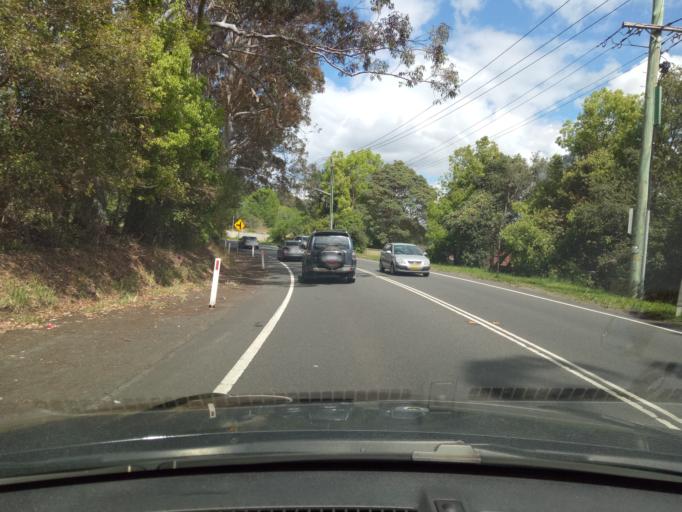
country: AU
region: New South Wales
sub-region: Gosford Shire
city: Narara
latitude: -33.3900
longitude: 151.3542
